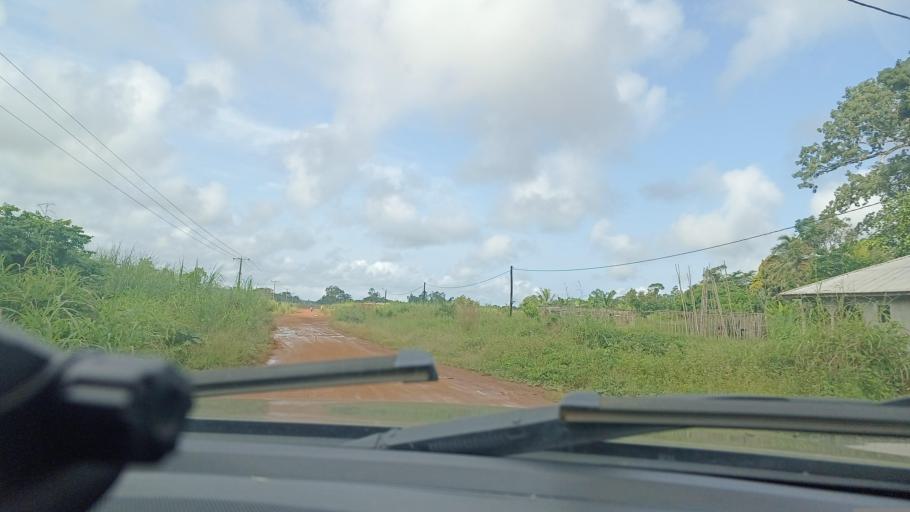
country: LR
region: Grand Cape Mount
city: Robertsport
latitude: 6.6871
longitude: -11.1199
